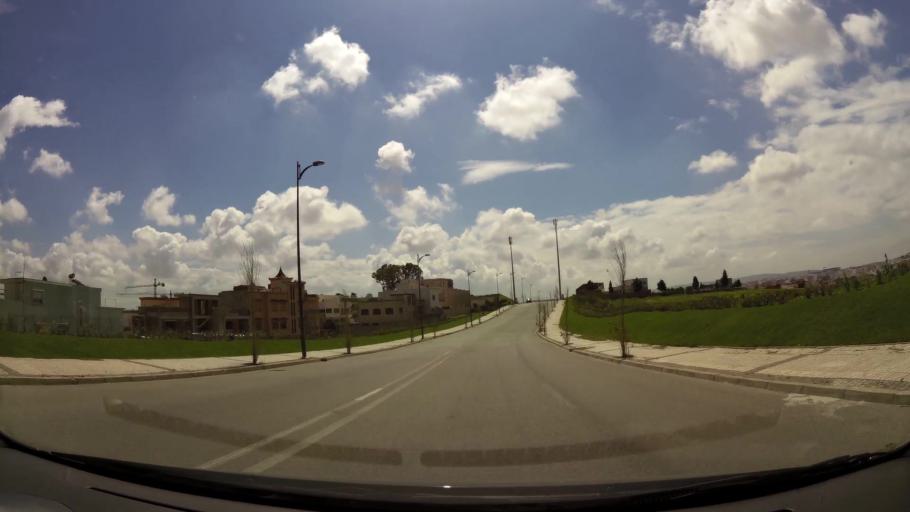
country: MA
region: Tanger-Tetouan
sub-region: Tanger-Assilah
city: Tangier
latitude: 35.7702
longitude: -5.8396
